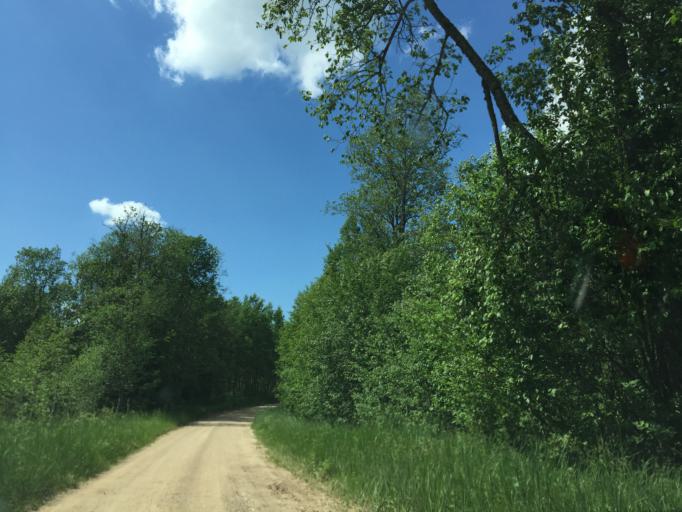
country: LV
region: Priekuli
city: Priekuli
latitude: 57.2308
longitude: 25.4280
